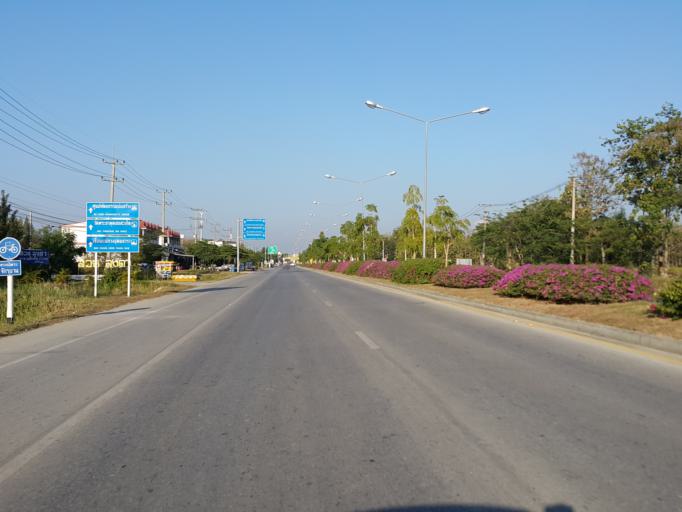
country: TH
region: Chiang Mai
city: San Kamphaeng
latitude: 18.7597
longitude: 99.0780
